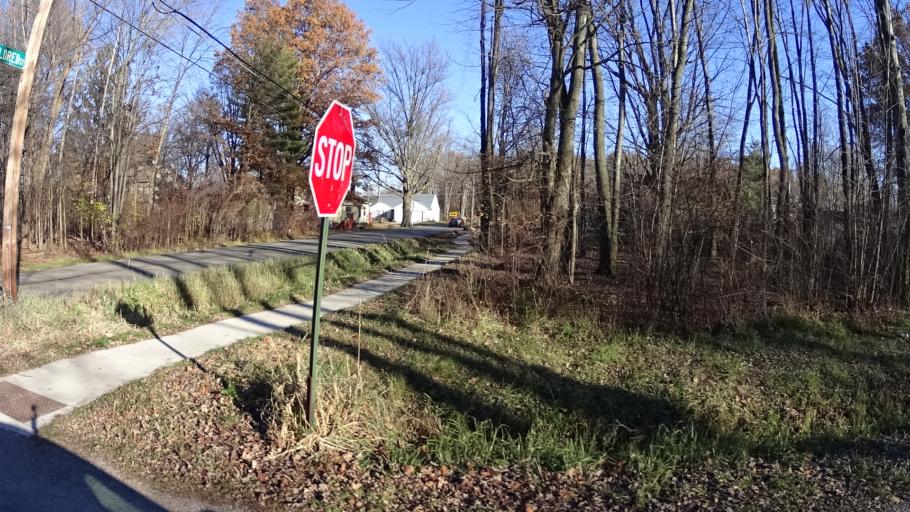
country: US
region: Ohio
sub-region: Lorain County
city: North Ridgeville
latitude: 41.3994
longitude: -82.0121
